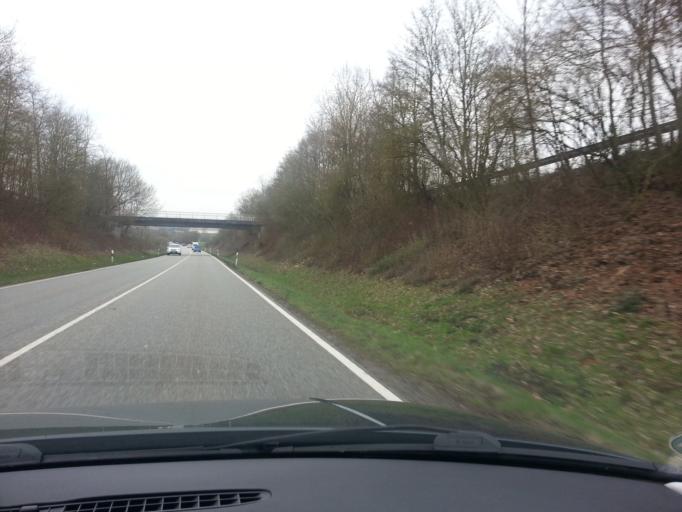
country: DE
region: Rheinland-Pfalz
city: Rodenbach
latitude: 49.4802
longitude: 7.6741
